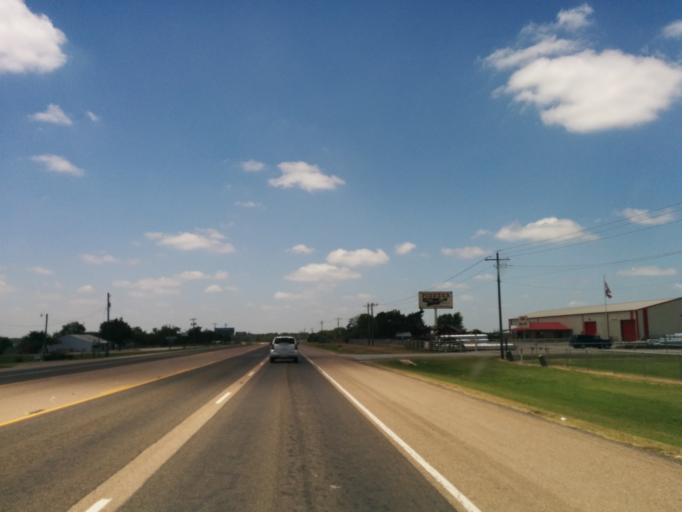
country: US
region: Texas
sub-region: Brazos County
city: Bryan
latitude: 30.7530
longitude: -96.3028
